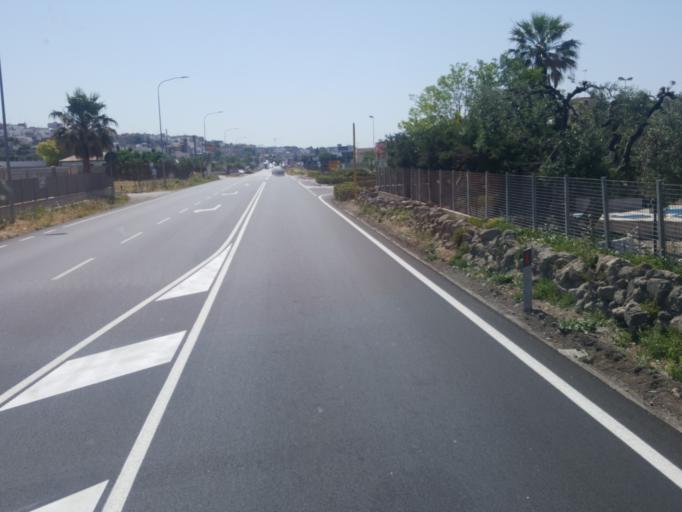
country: IT
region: Apulia
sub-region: Provincia di Taranto
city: Massafra
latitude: 40.5894
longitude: 17.1006
